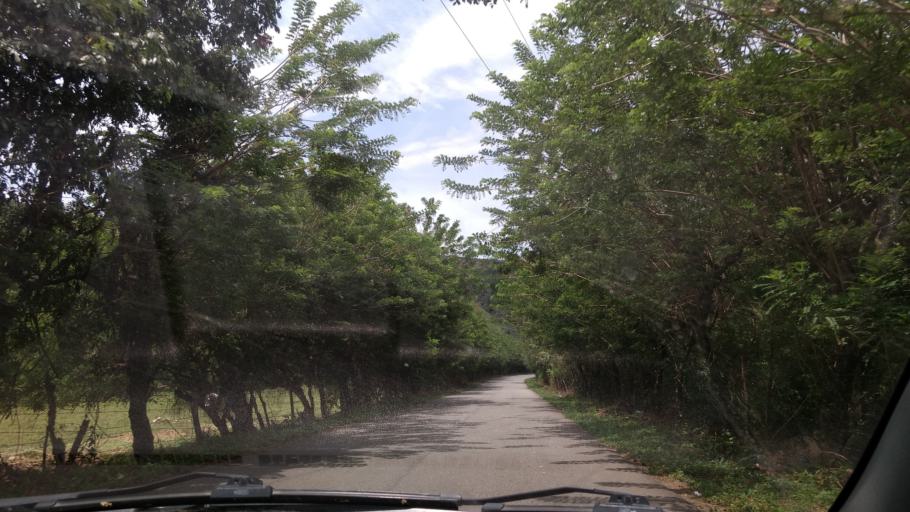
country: CO
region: Cauca
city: Buenos Aires
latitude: 3.0732
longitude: -76.6532
